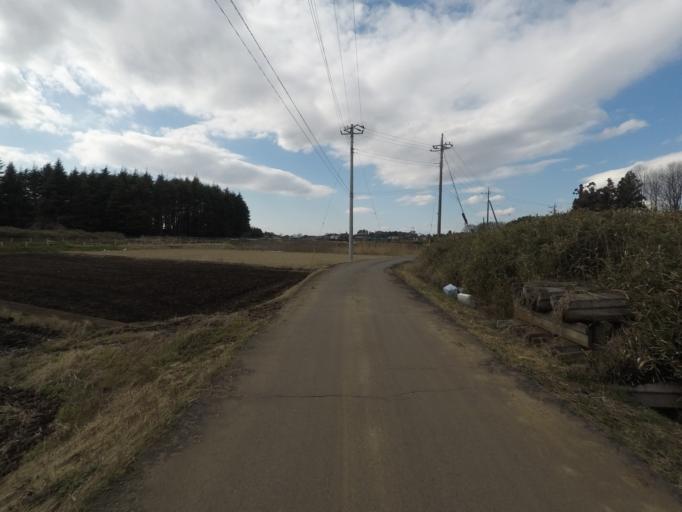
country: JP
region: Ibaraki
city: Ushiku
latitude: 36.0142
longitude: 140.1139
